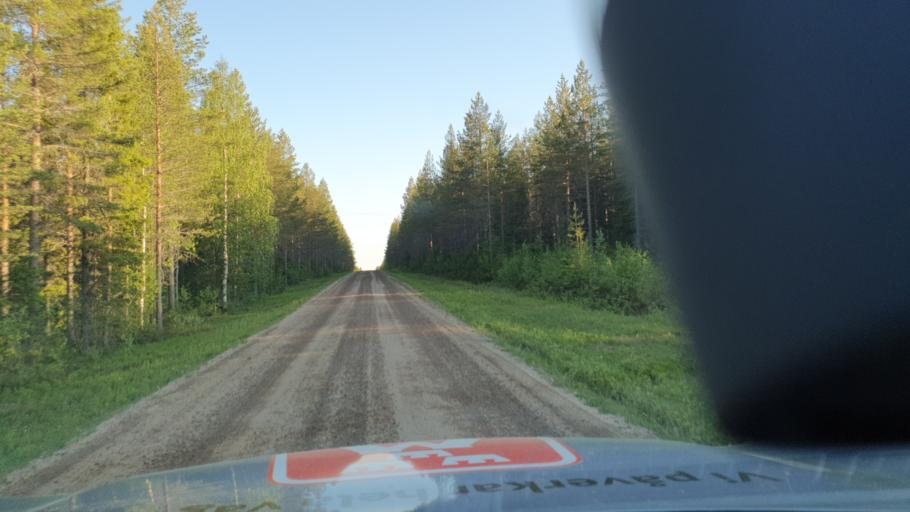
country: FI
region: Lapland
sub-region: Torniolaakso
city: Ylitornio
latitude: 66.0778
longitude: 23.6882
